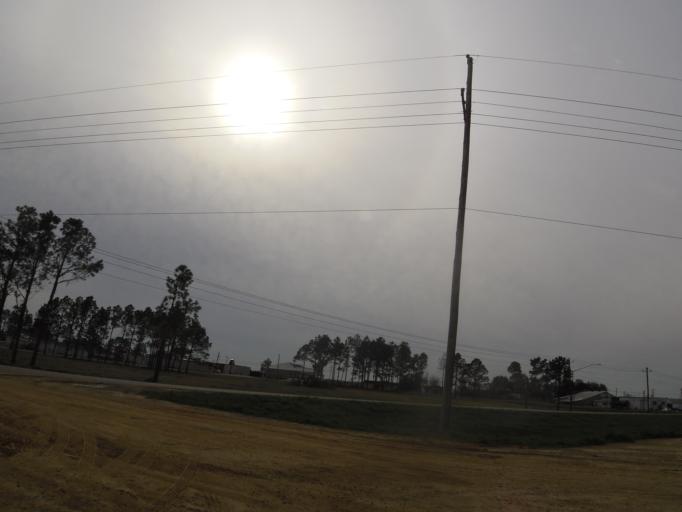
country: US
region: Georgia
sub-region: Seminole County
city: Donalsonville
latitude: 31.0437
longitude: -84.8872
